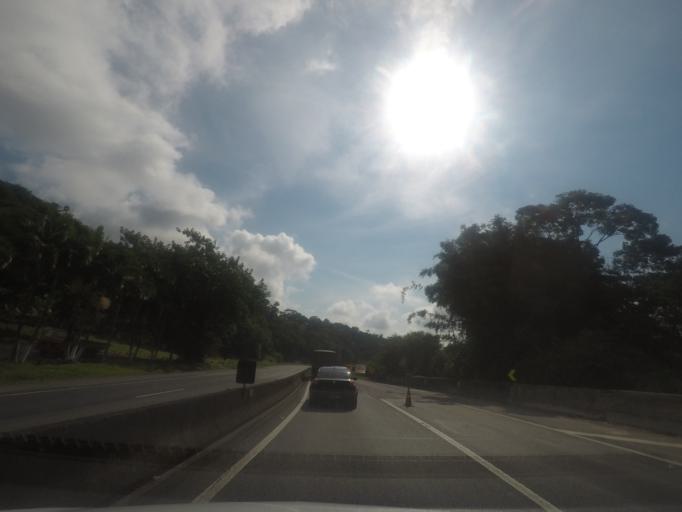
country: BR
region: Parana
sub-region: Antonina
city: Antonina
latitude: -25.5704
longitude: -48.8146
